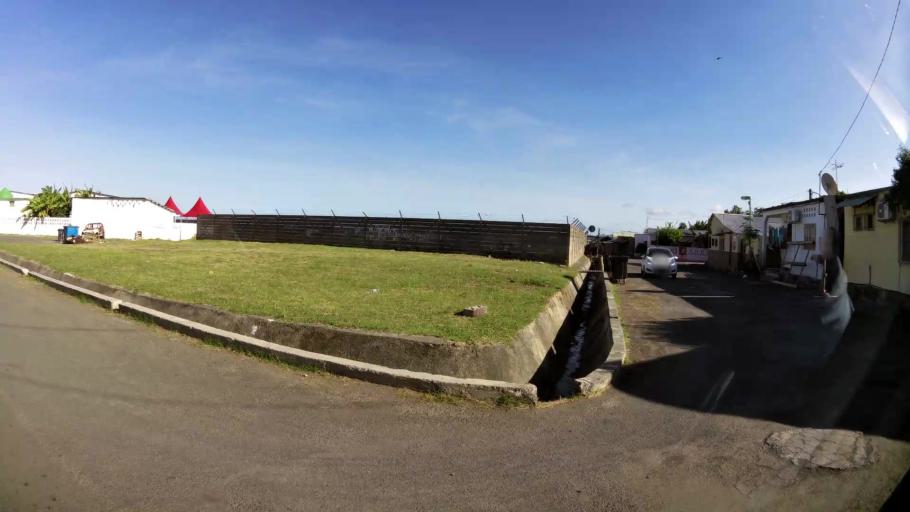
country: YT
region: Pamandzi
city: Pamandzi
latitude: -12.8000
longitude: 45.2769
